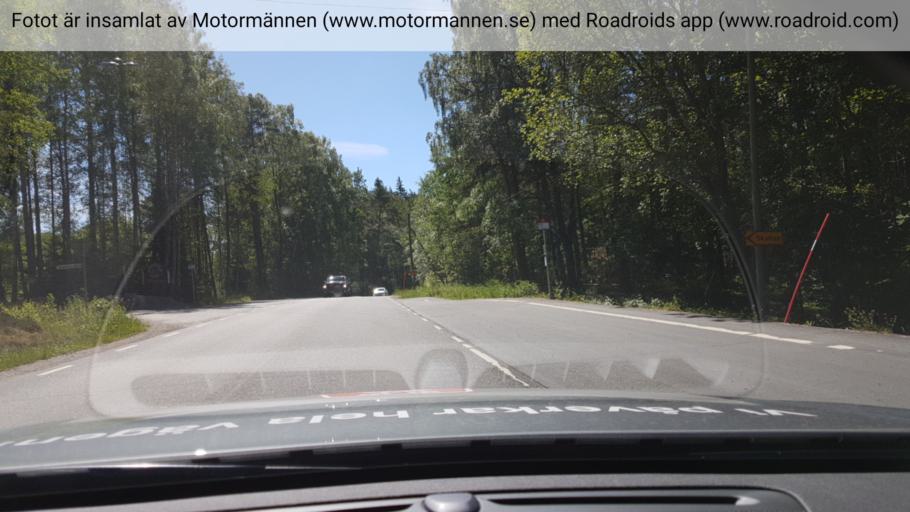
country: SE
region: Stockholm
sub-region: Haninge Kommun
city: Haninge
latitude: 59.1633
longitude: 18.1819
